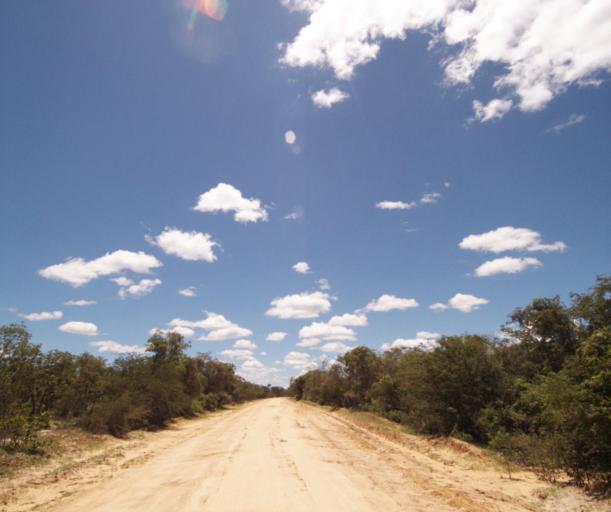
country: BR
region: Bahia
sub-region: Carinhanha
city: Carinhanha
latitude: -14.2116
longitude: -43.9322
